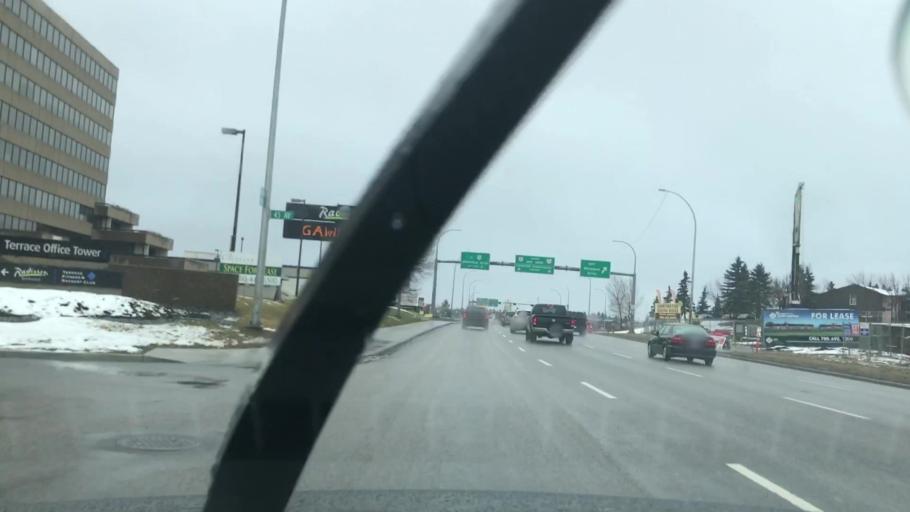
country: CA
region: Alberta
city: Edmonton
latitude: 53.4832
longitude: -113.4949
